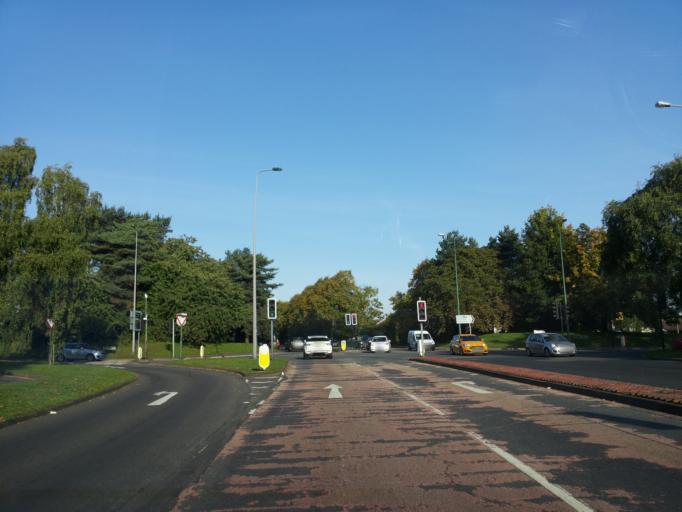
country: GB
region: England
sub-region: Solihull
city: Solihull
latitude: 52.4172
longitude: -1.7621
